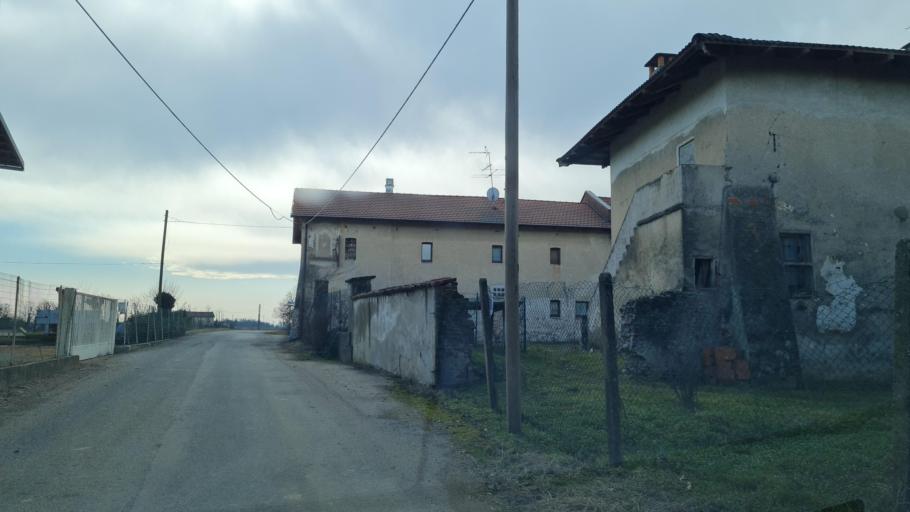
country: IT
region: Piedmont
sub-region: Provincia di Vercelli
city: Buronzo
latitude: 45.4688
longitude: 8.2475
